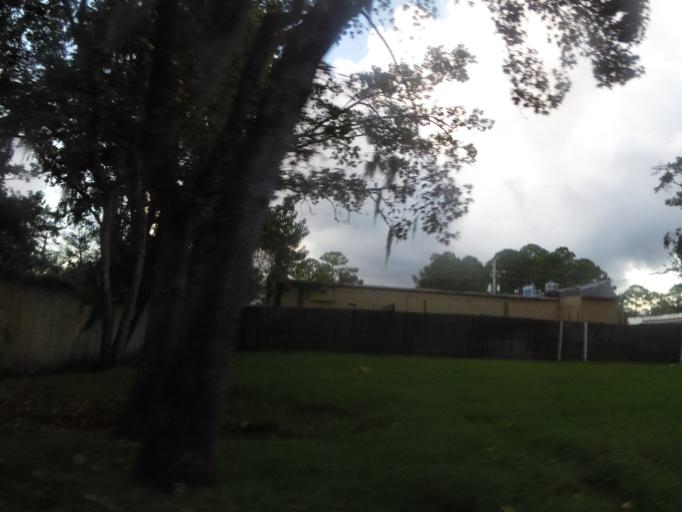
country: US
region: Florida
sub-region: Duval County
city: Jacksonville
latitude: 30.2326
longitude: -81.6044
